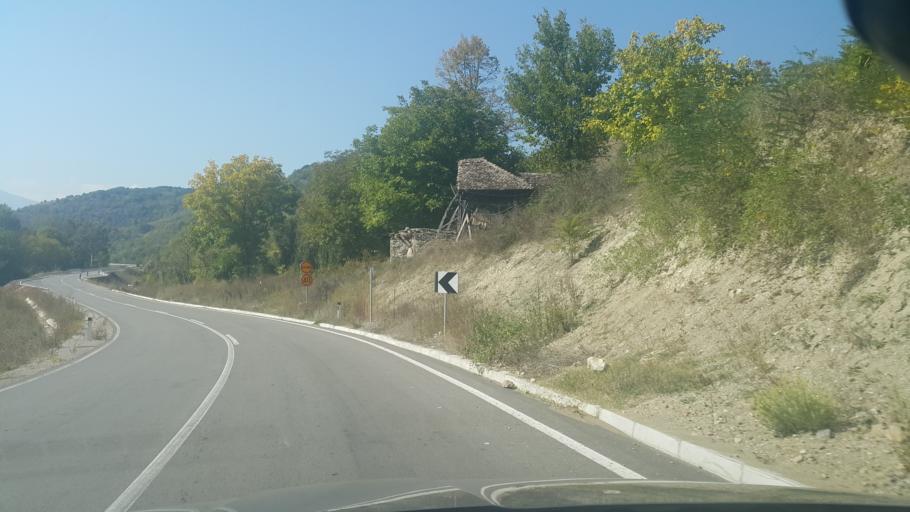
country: RS
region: Central Serbia
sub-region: Pirotski Okrug
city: Bela Palanka
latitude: 43.2386
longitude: 22.4082
